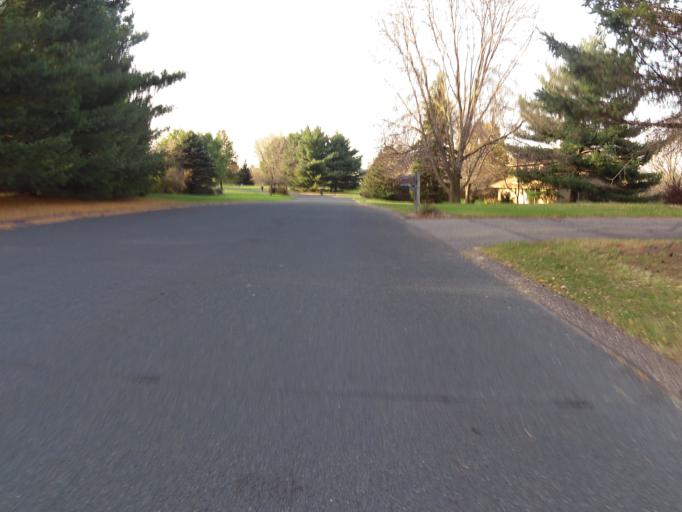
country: US
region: Minnesota
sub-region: Washington County
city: Lake Elmo
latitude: 44.9654
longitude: -92.8749
